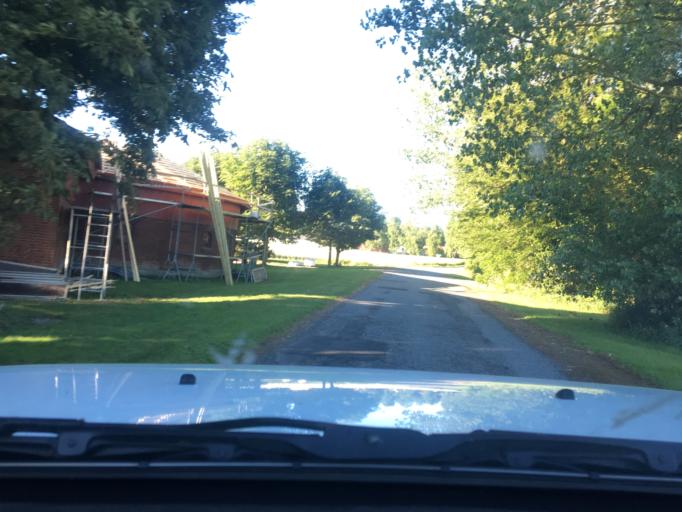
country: DK
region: Central Jutland
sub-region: Randers Kommune
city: Randers
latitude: 56.4108
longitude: 10.0542
